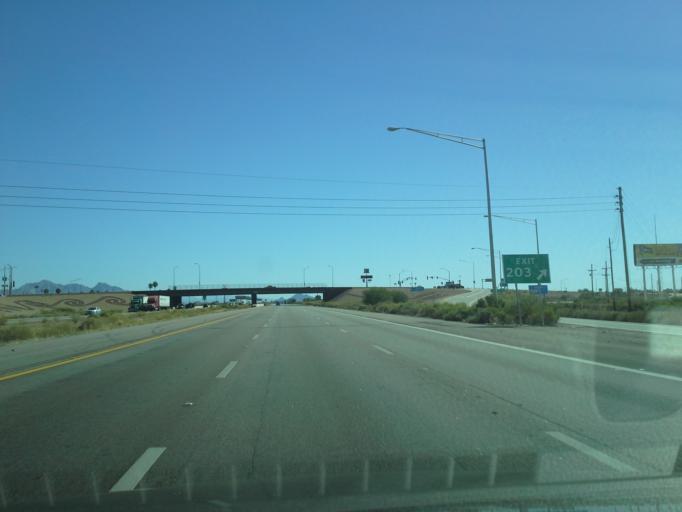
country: US
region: Arizona
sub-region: Pinal County
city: Arizona City
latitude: 32.7787
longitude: -111.6222
